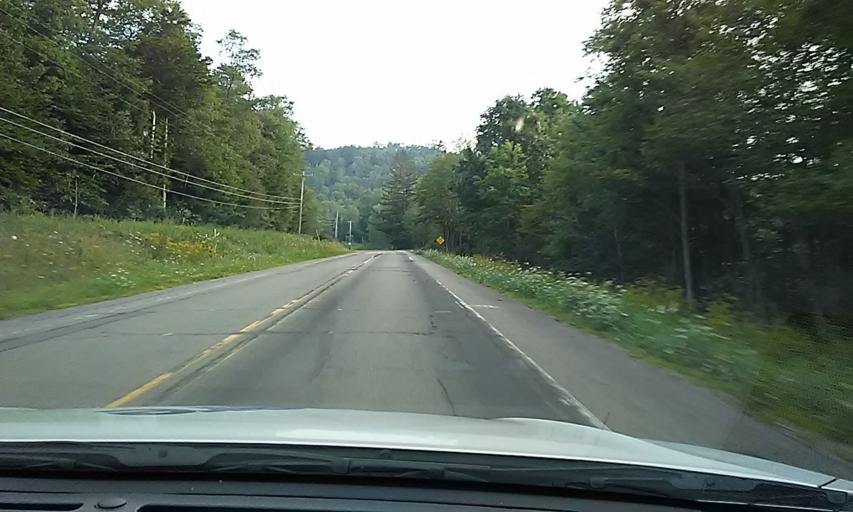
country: US
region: Pennsylvania
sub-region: McKean County
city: Kane
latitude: 41.6299
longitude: -78.8245
